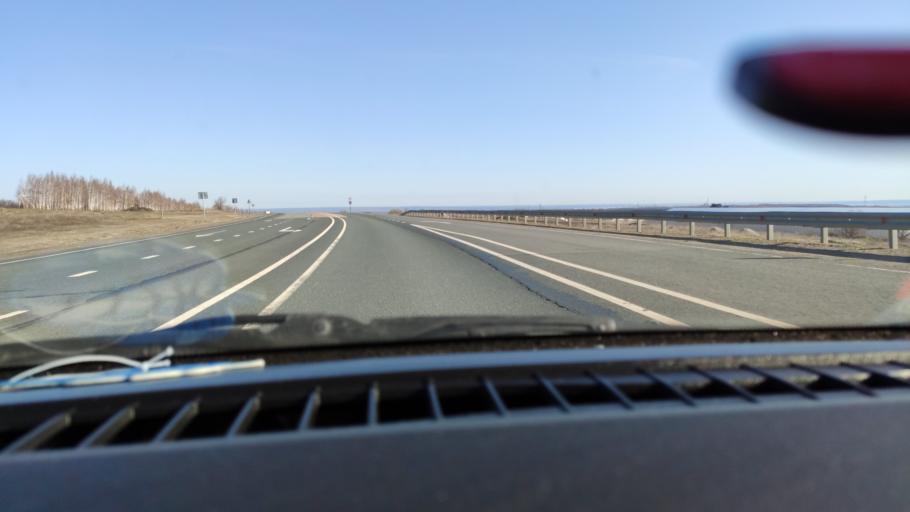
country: RU
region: Samara
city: Syzran'
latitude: 52.9565
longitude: 48.3078
